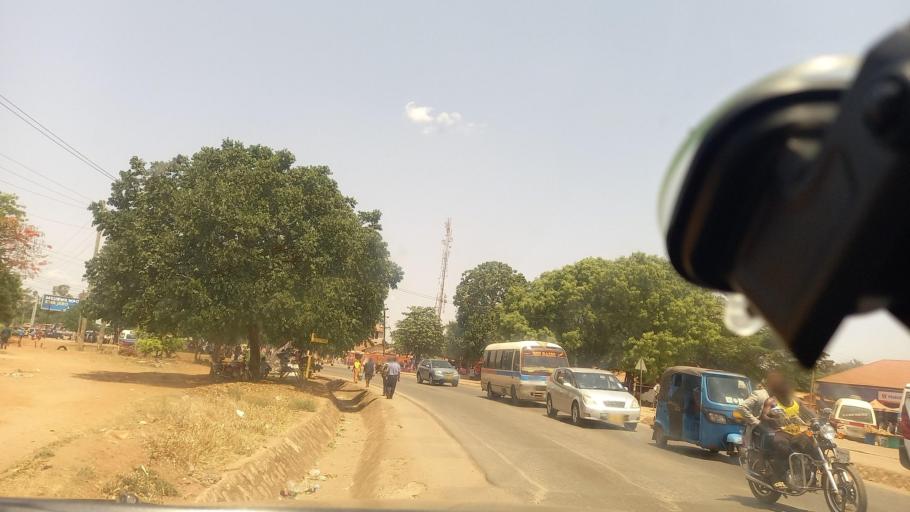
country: TZ
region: Morogoro
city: Morogoro
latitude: -6.8213
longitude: 37.6641
